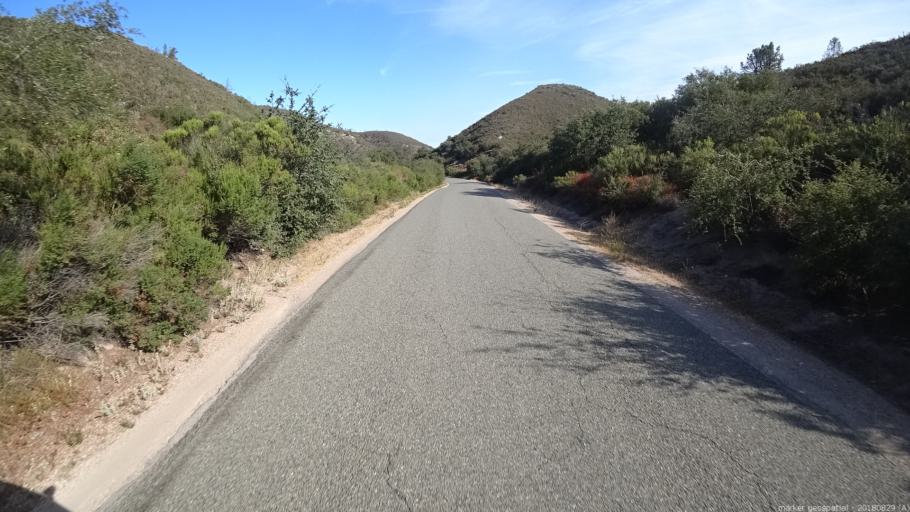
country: US
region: California
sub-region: Monterey County
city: King City
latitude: 36.0174
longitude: -121.0678
